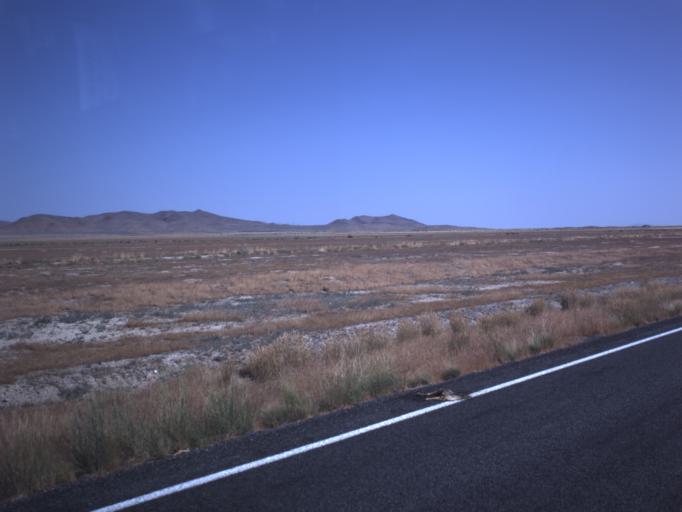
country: US
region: Utah
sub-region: Millard County
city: Delta
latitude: 38.9694
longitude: -112.7997
